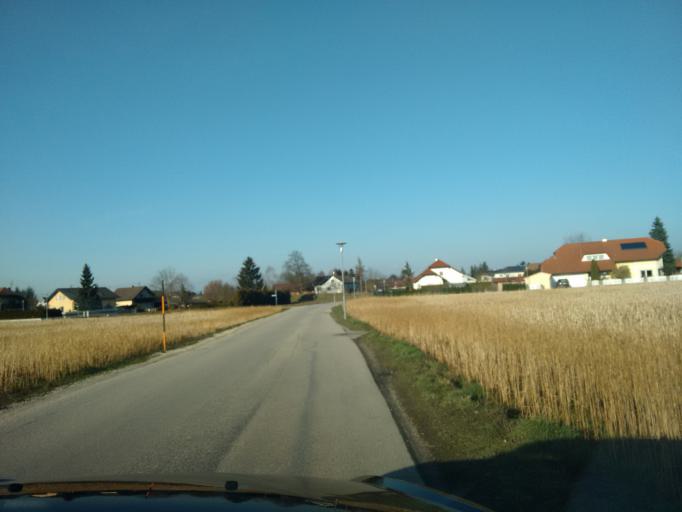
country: AT
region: Upper Austria
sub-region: Wels-Land
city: Marchtrenk
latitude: 48.1960
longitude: 14.0965
